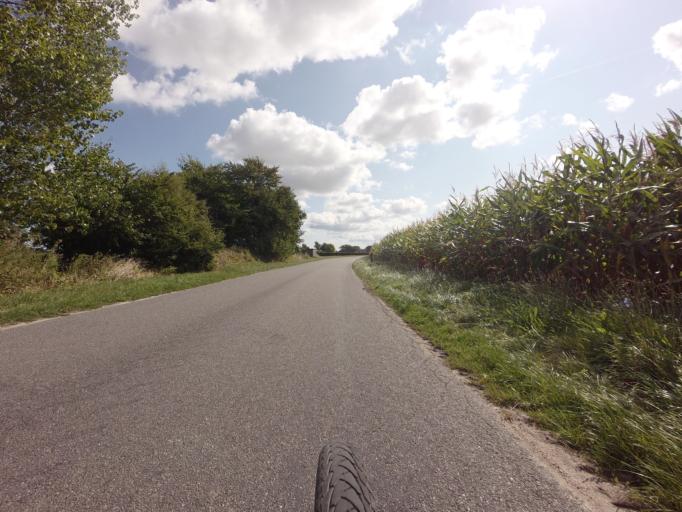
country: DK
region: Zealand
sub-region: Vordingborg Kommune
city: Stege
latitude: 54.9741
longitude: 12.3734
